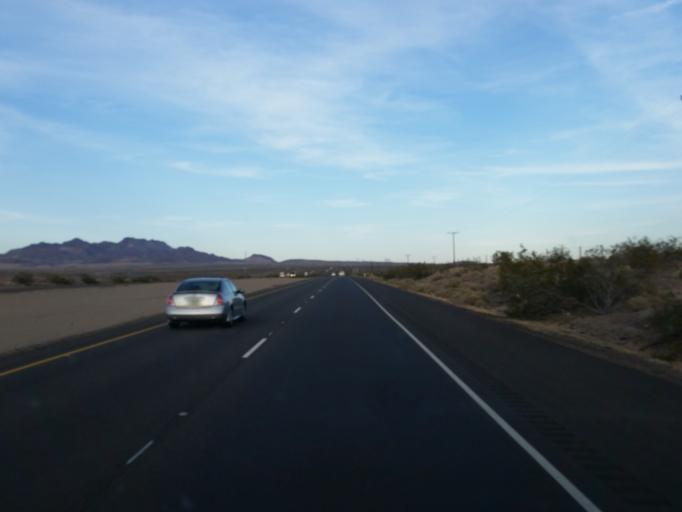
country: US
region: California
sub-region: San Bernardino County
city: Fort Irwin
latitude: 34.7814
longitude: -116.4075
